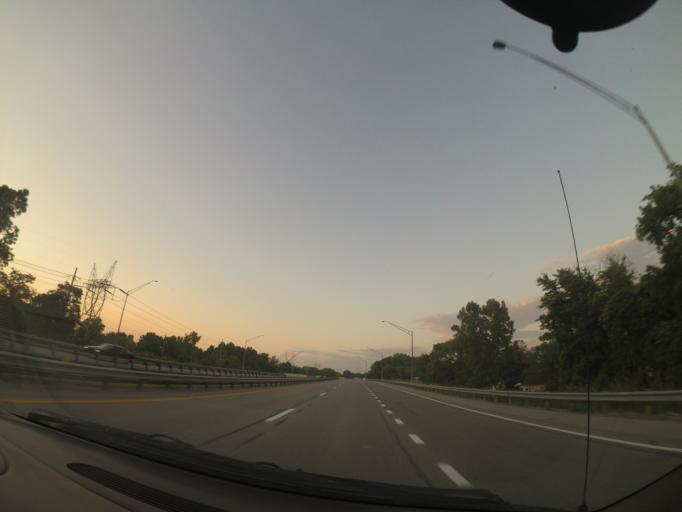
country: US
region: Ohio
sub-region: Lake County
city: Painesville
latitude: 41.7321
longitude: -81.2567
